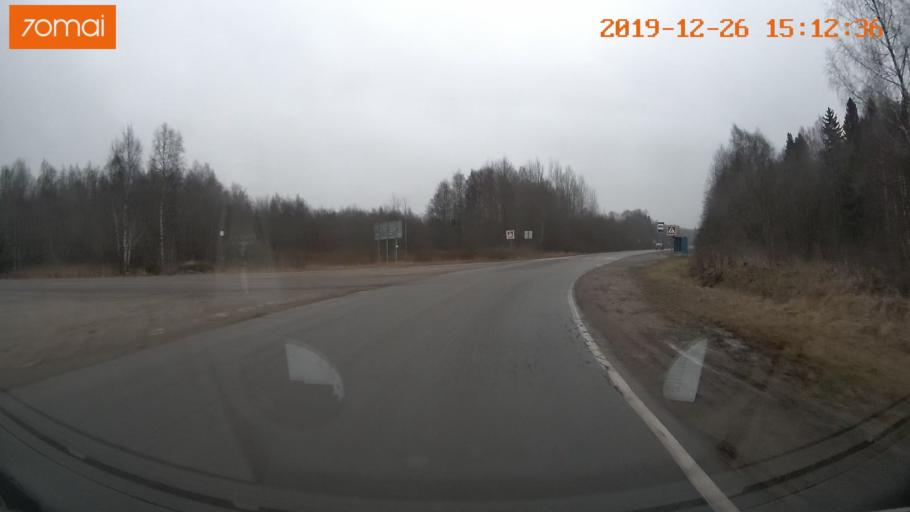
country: RU
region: Jaroslavl
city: Rybinsk
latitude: 58.1266
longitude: 38.8785
